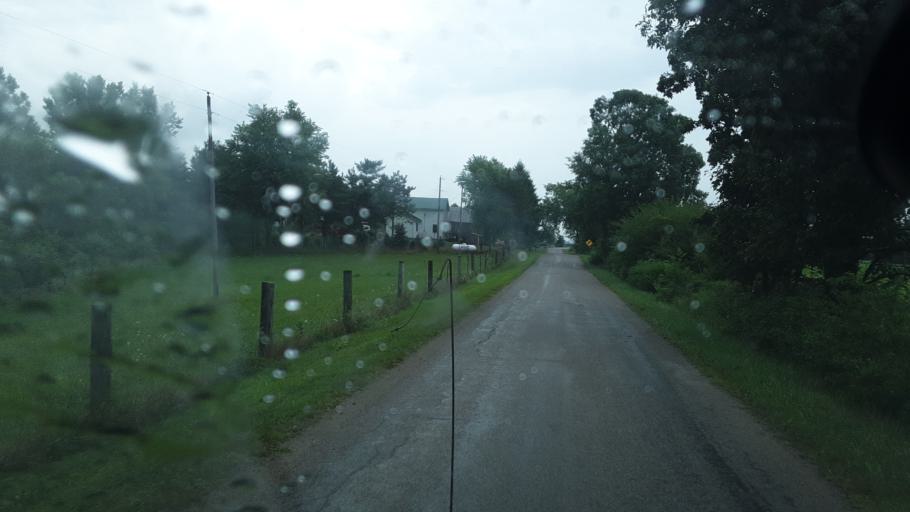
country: US
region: Ohio
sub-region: Williams County
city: Edgerton
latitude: 41.5245
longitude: -84.8081
